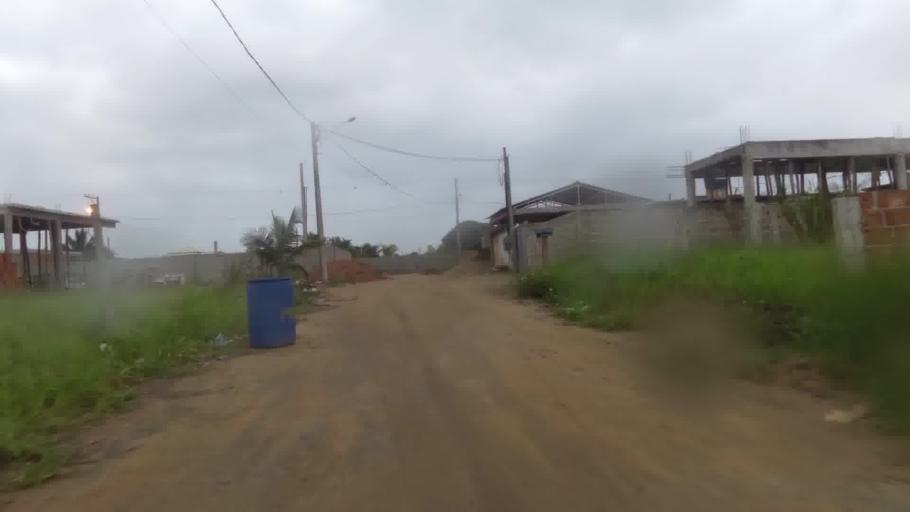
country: BR
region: Espirito Santo
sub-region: Marataizes
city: Marataizes
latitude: -21.0418
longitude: -40.8418
